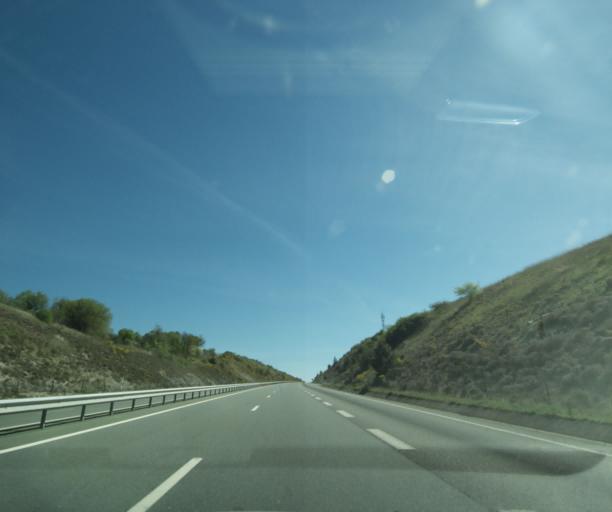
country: FR
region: Midi-Pyrenees
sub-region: Departement du Lot
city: Le Vigan
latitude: 44.7164
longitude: 1.5673
